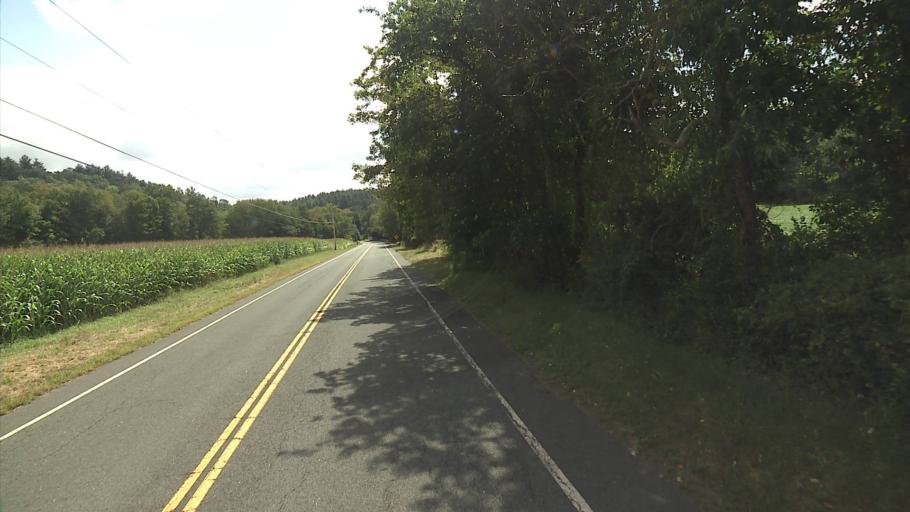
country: US
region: Connecticut
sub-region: Hartford County
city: North Granby
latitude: 42.0220
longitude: -72.8591
